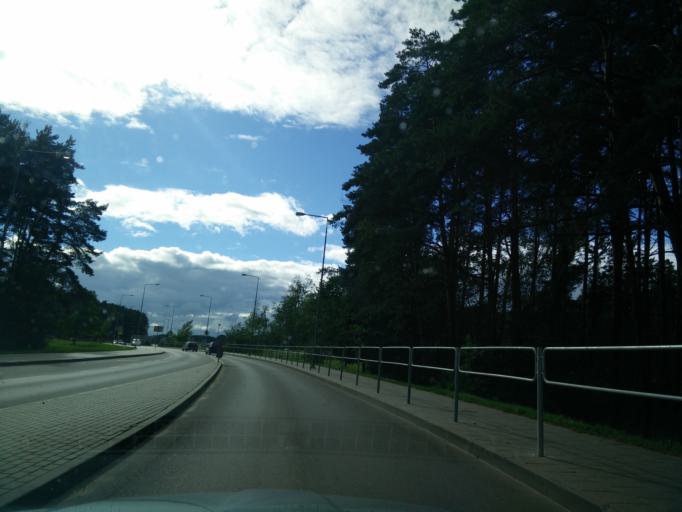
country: LT
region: Vilnius County
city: Lazdynai
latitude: 54.6698
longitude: 25.2104
